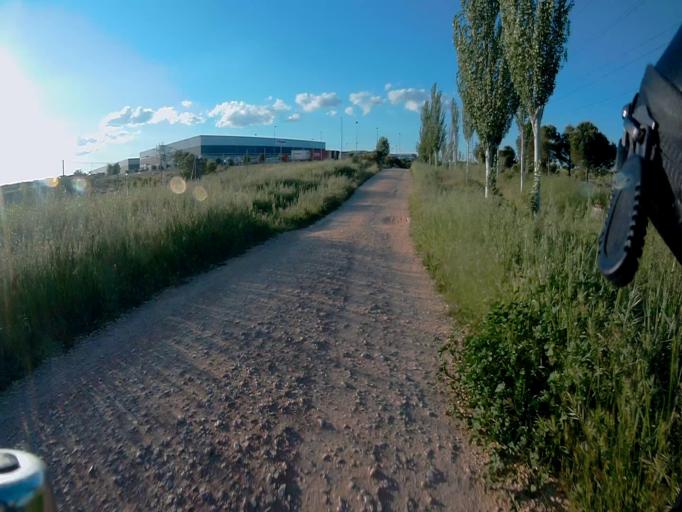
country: ES
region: Madrid
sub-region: Provincia de Madrid
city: Fuenlabrada
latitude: 40.3031
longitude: -3.7990
